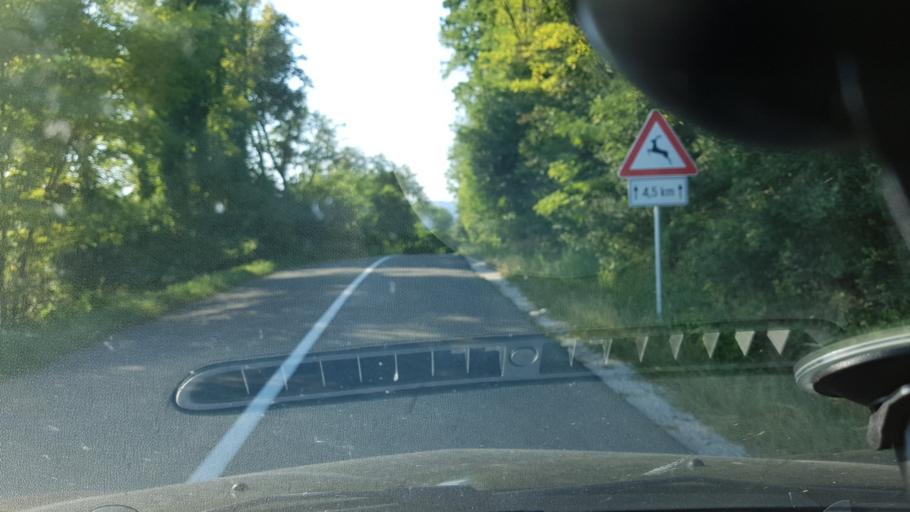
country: SI
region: Bistrica ob Sotli
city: Bistrica ob Sotli
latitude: 45.9995
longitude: 15.7189
